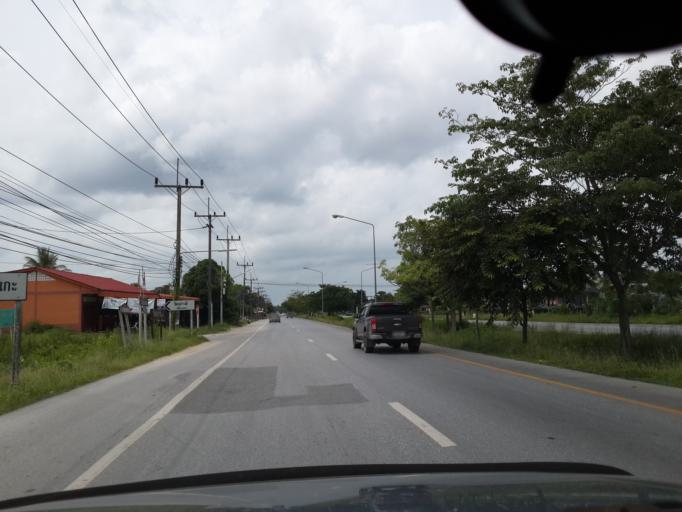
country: TH
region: Pattani
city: Yaring
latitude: 6.8676
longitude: 101.3362
